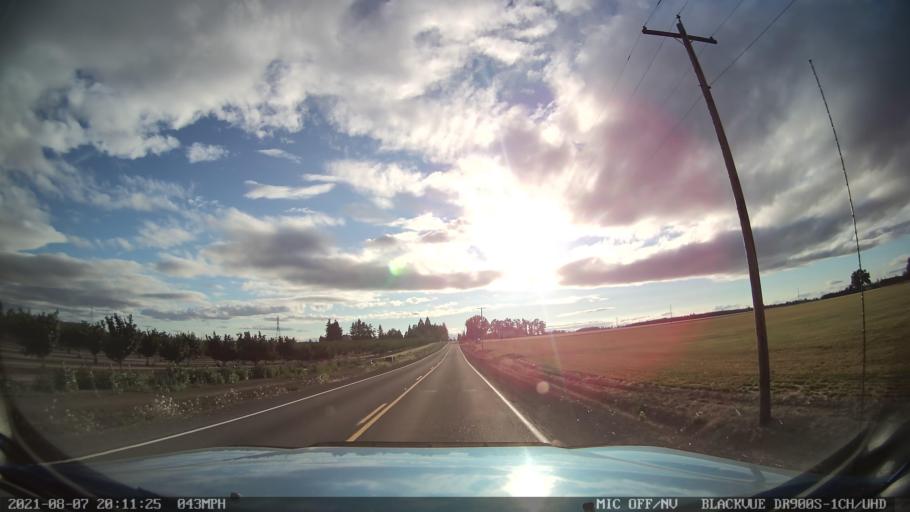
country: US
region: Oregon
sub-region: Marion County
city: Hayesville
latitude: 44.9583
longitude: -122.8905
